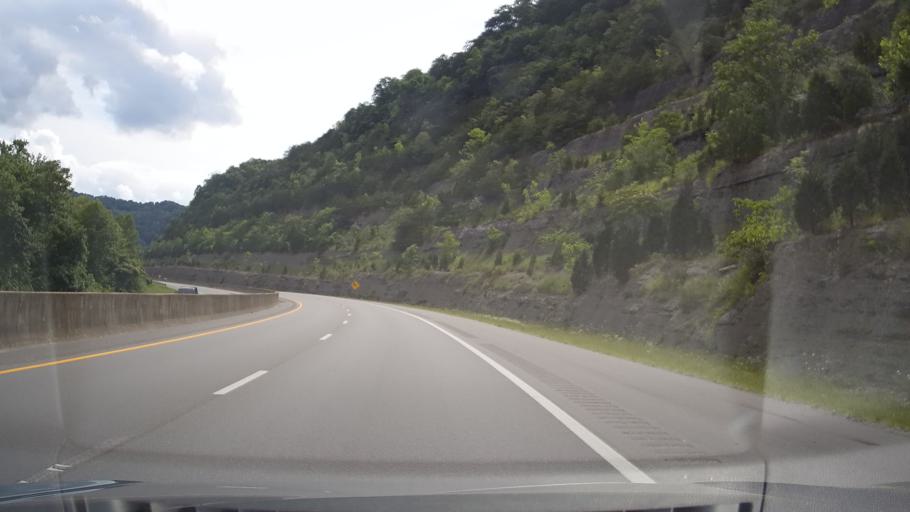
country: US
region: Kentucky
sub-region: Pike County
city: Coal Run Village
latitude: 37.5421
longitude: -82.5896
